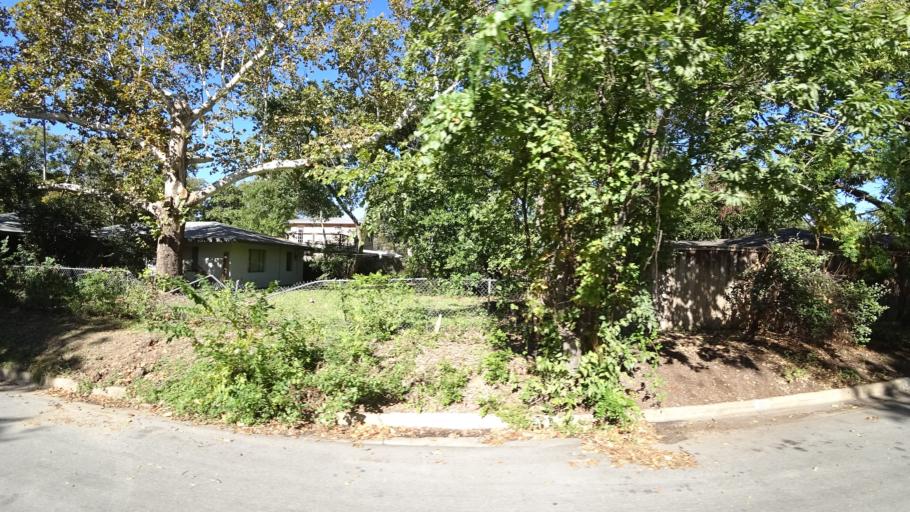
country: US
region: Texas
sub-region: Travis County
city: Austin
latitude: 30.3005
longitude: -97.7096
